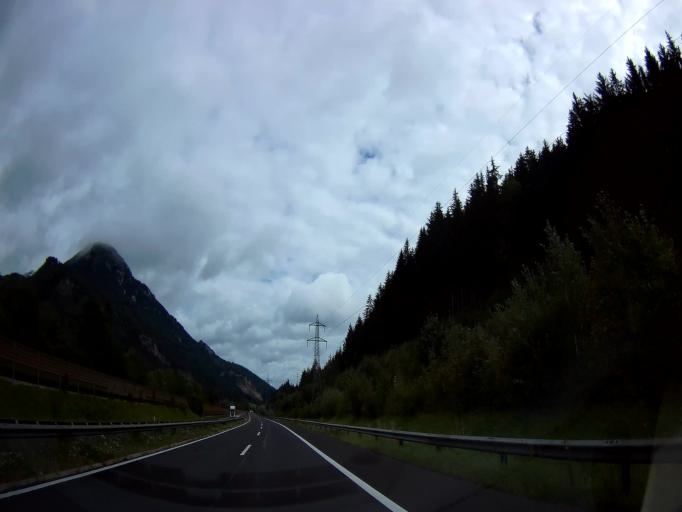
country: AT
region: Styria
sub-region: Politischer Bezirk Leoben
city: Mautern in Steiermark
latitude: 47.3951
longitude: 14.8325
